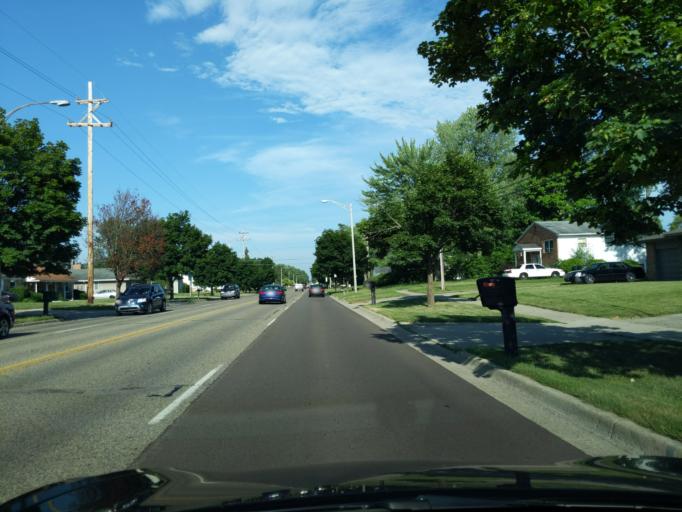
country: US
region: Michigan
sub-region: Ingham County
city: East Lansing
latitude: 42.7469
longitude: -84.4591
